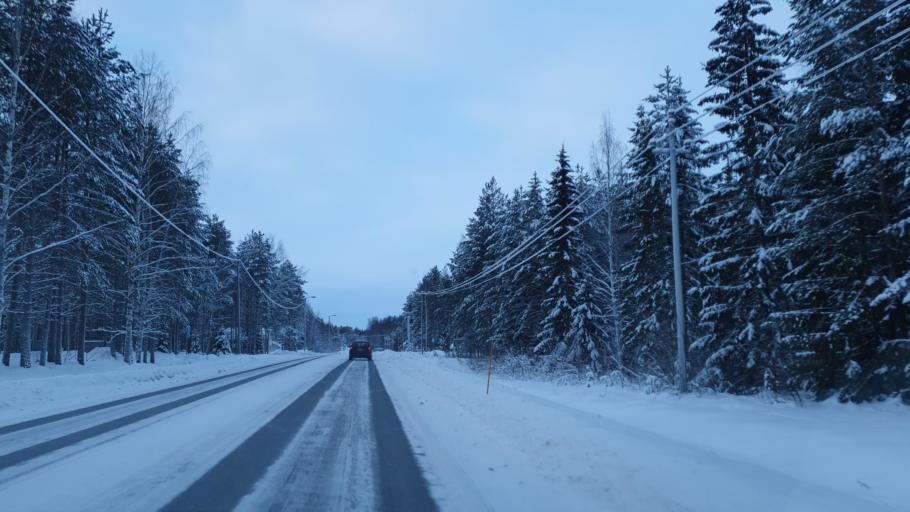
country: FI
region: Northern Ostrobothnia
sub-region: Oulu
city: Haukipudas
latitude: 65.1949
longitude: 25.3756
